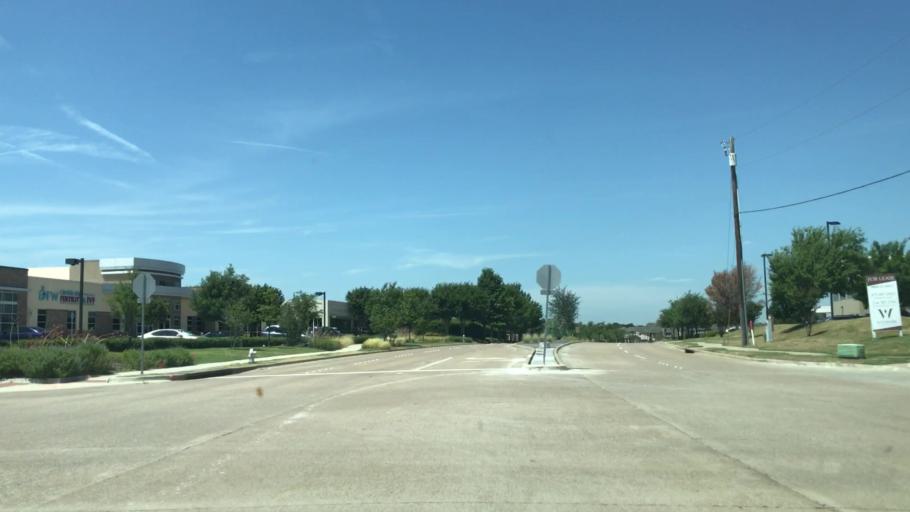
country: US
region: Texas
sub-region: Collin County
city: Allen
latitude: 33.1110
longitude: -96.6788
